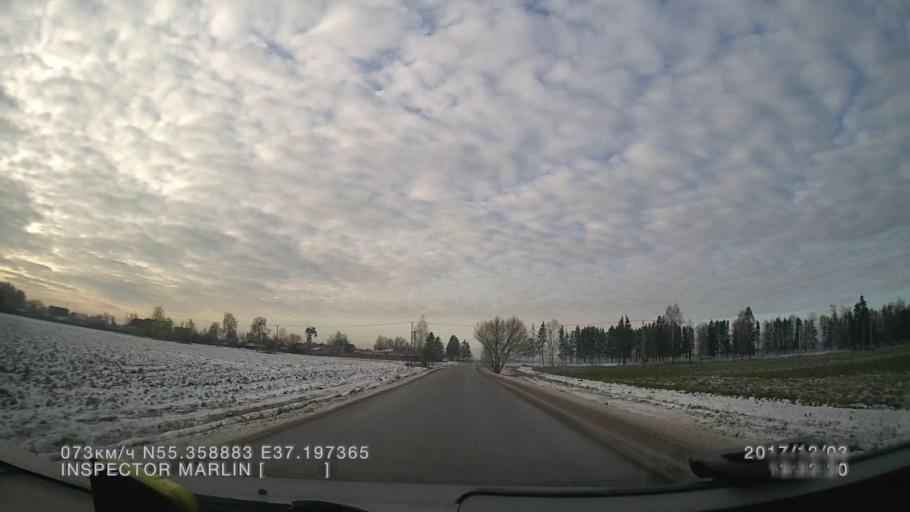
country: RU
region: Moskovskaya
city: Troitsk
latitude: 55.3587
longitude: 37.1977
